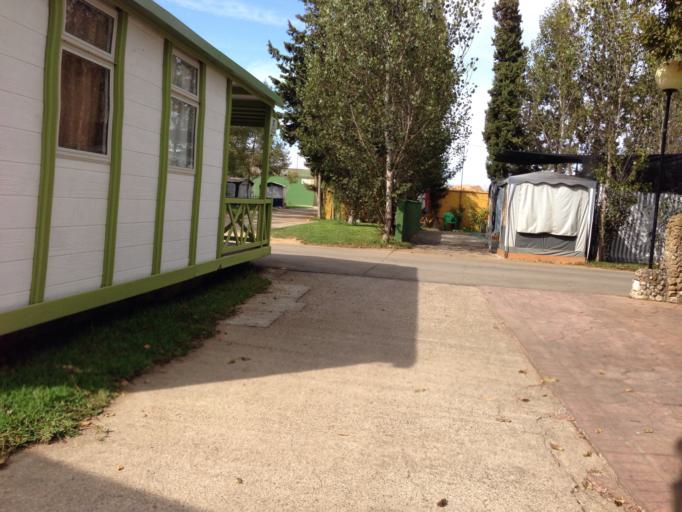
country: ES
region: Andalusia
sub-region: Provincia de Cadiz
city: Conil de la Frontera
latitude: 36.3123
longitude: -6.1130
